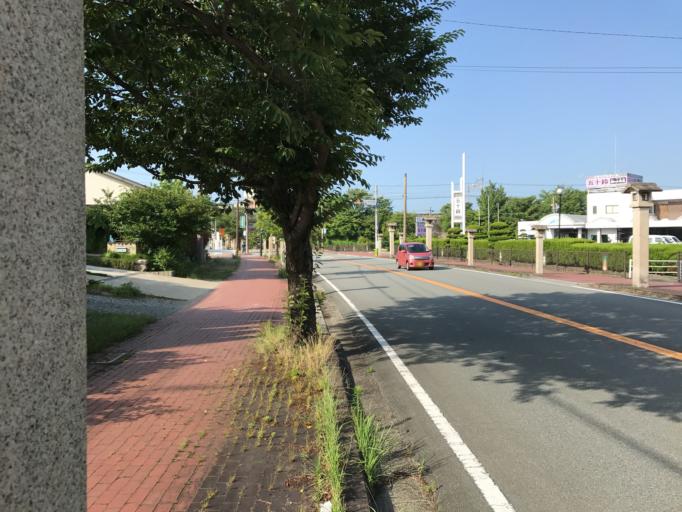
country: JP
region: Mie
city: Ise
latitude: 34.4744
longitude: 136.7282
